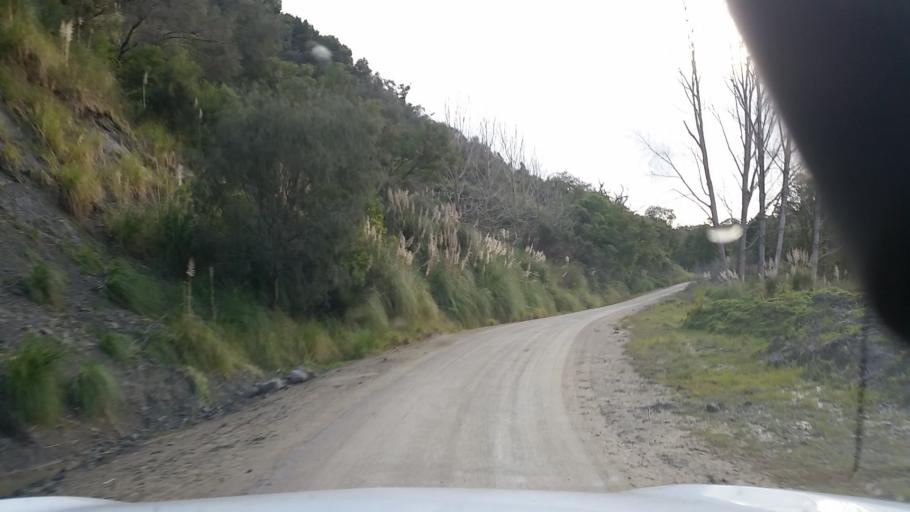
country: NZ
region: Taranaki
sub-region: South Taranaki District
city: Patea
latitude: -39.5569
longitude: 174.8044
